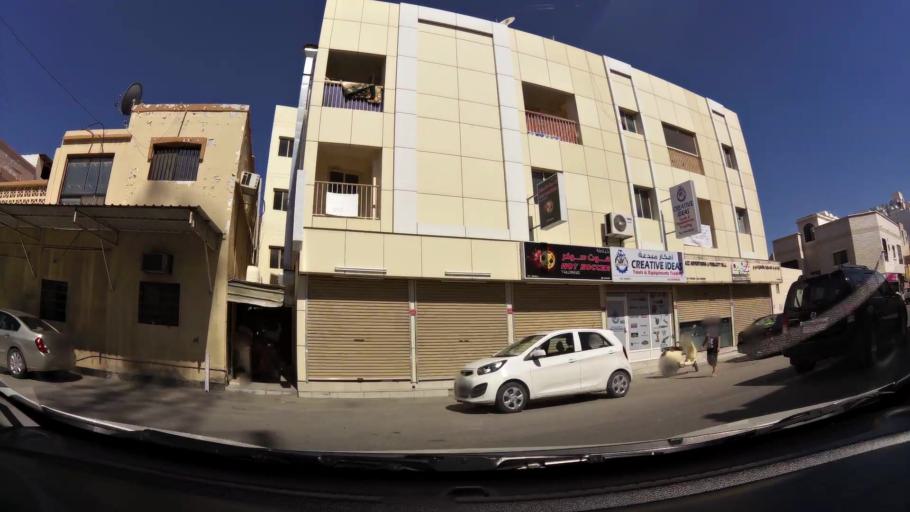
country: BH
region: Muharraq
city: Al Muharraq
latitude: 26.2440
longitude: 50.6148
